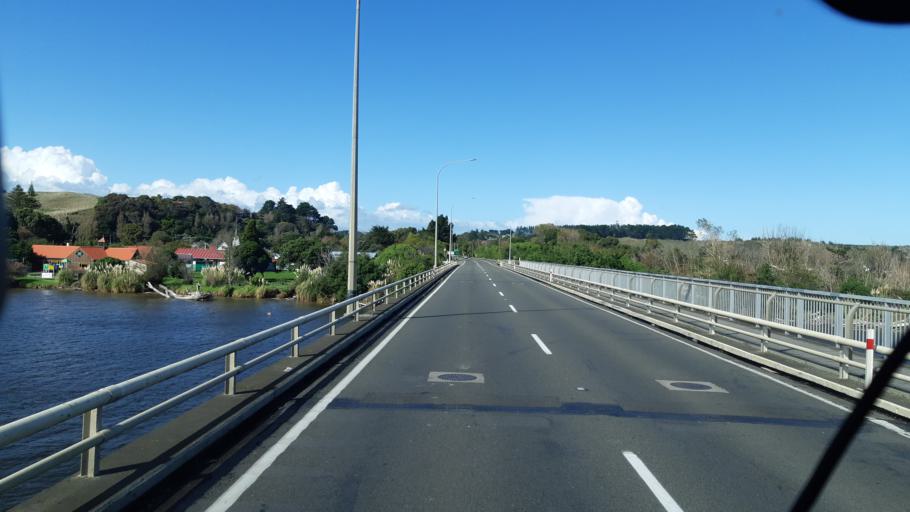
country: NZ
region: Manawatu-Wanganui
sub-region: Wanganui District
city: Wanganui
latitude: -39.9452
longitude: 175.0464
